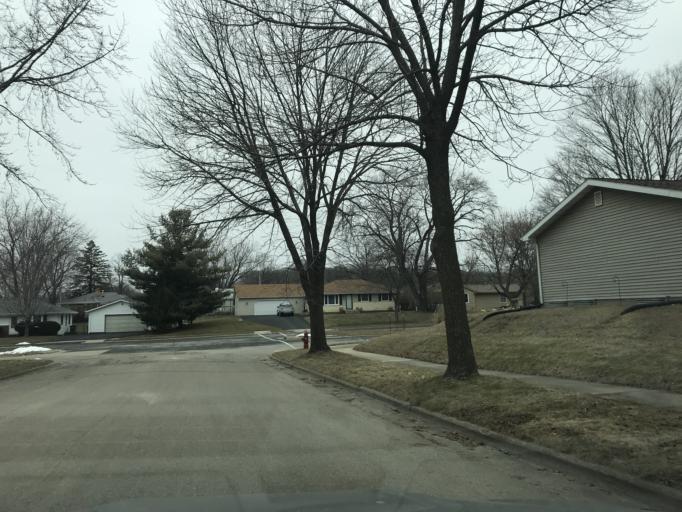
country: US
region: Wisconsin
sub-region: Dane County
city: Monona
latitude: 43.0976
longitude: -89.3082
